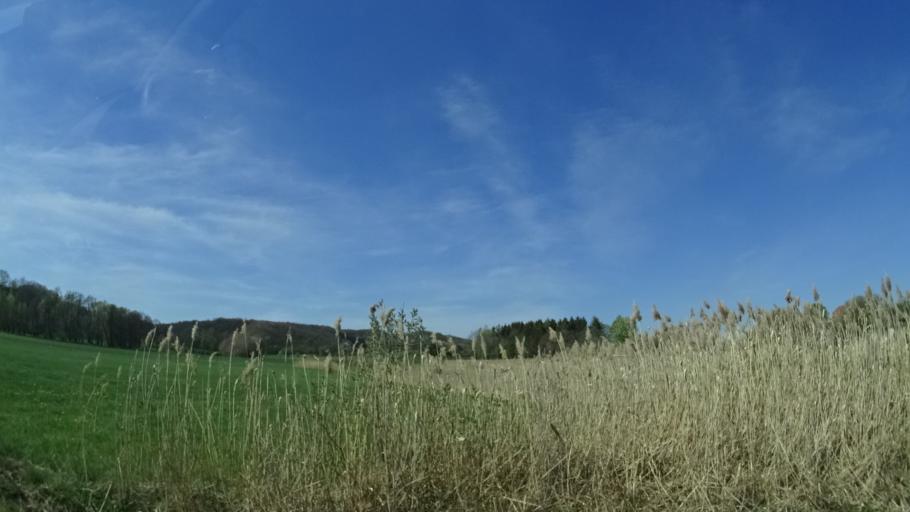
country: DE
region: Thuringia
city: Veilsdorf
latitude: 50.3032
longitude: 10.7983
